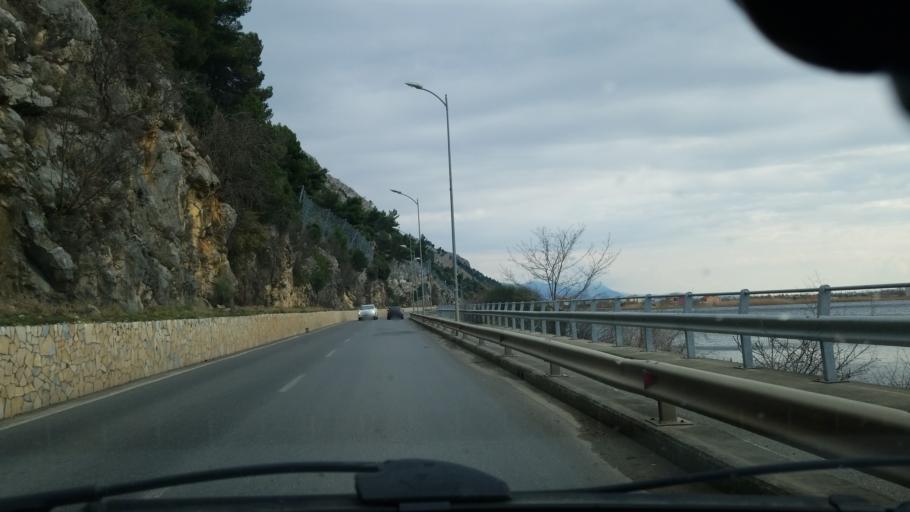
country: AL
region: Lezhe
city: Shengjin
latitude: 41.8048
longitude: 19.6129
